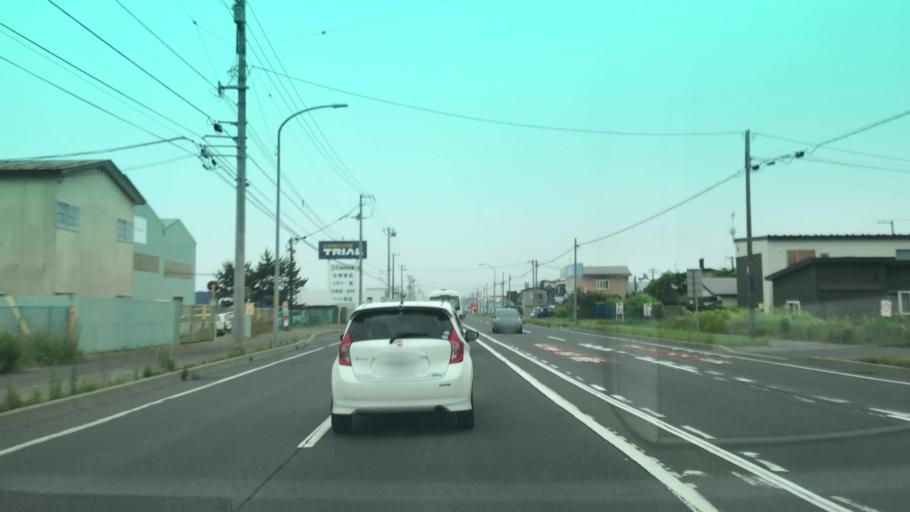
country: JP
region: Hokkaido
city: Muroran
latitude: 42.3813
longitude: 141.0739
